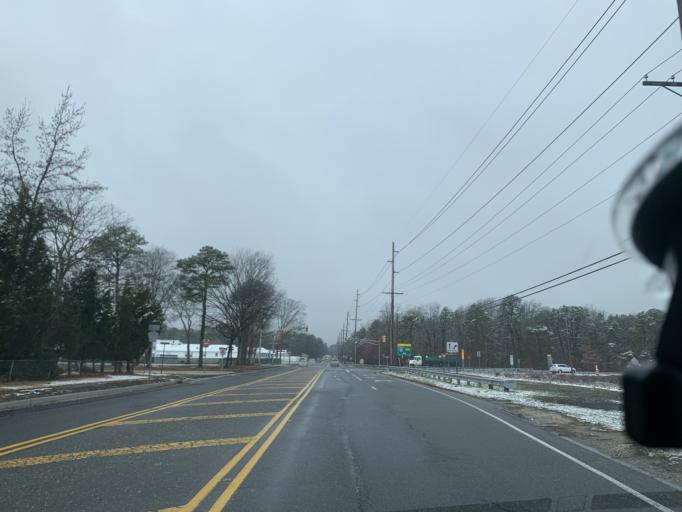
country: US
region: New Jersey
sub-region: Atlantic County
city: Pomona
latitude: 39.4347
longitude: -74.5903
